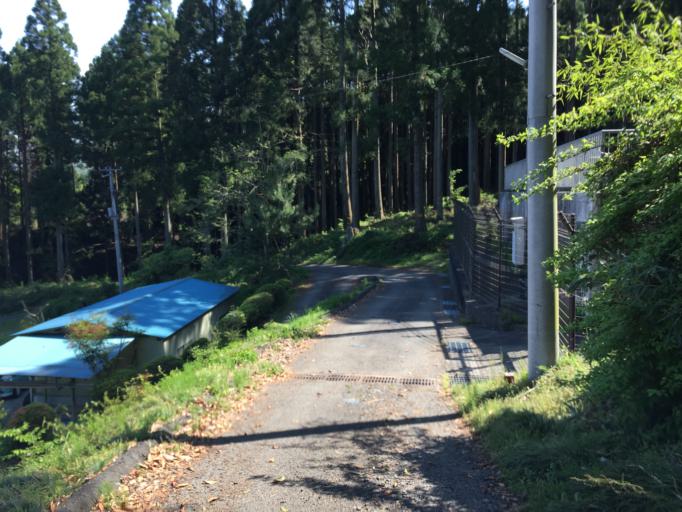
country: JP
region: Fukushima
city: Iwaki
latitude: 37.0559
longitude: 140.7899
